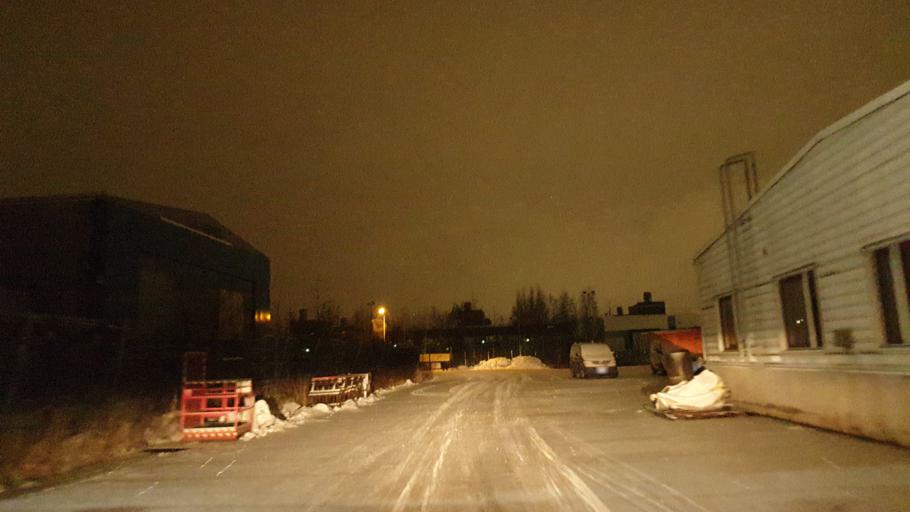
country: FI
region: Northern Ostrobothnia
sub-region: Oulu
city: Oulu
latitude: 64.9926
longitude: 25.4542
